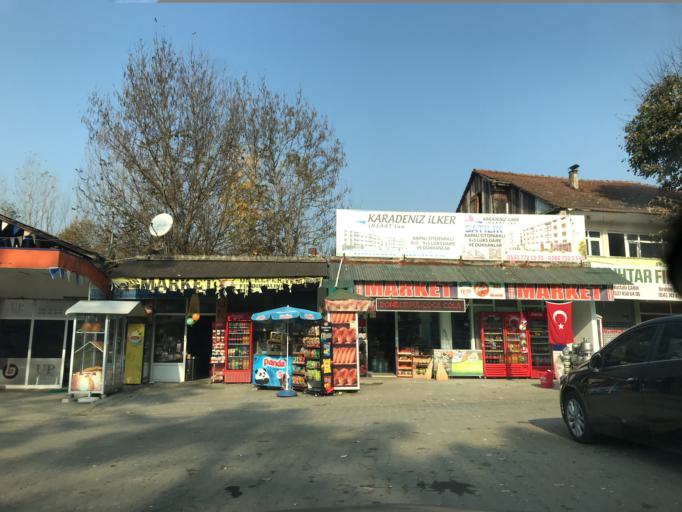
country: TR
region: Duzce
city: Cumayeri
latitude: 40.9082
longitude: 30.9503
